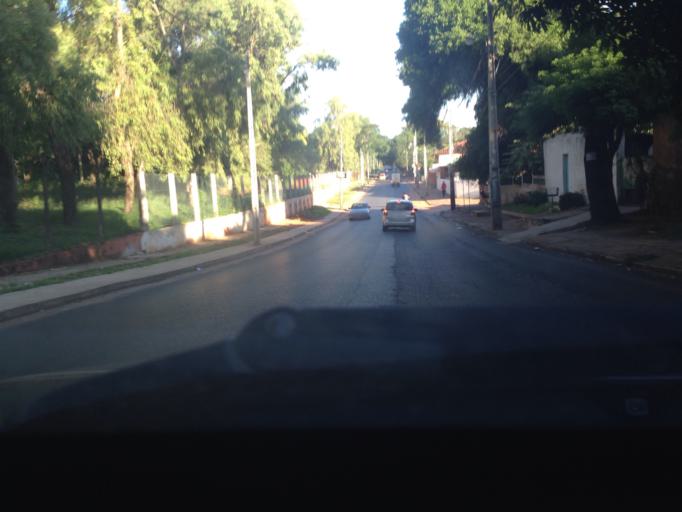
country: PY
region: Central
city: Lambare
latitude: -25.3195
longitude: -57.5893
